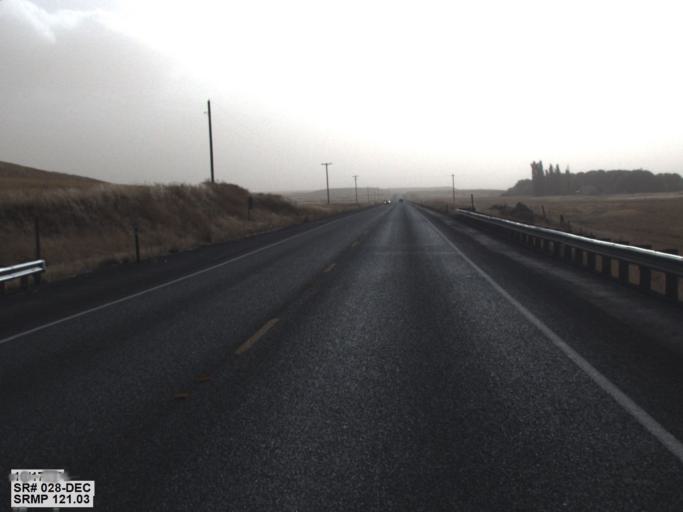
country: US
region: Washington
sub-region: Lincoln County
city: Davenport
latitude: 47.5179
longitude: -118.2148
